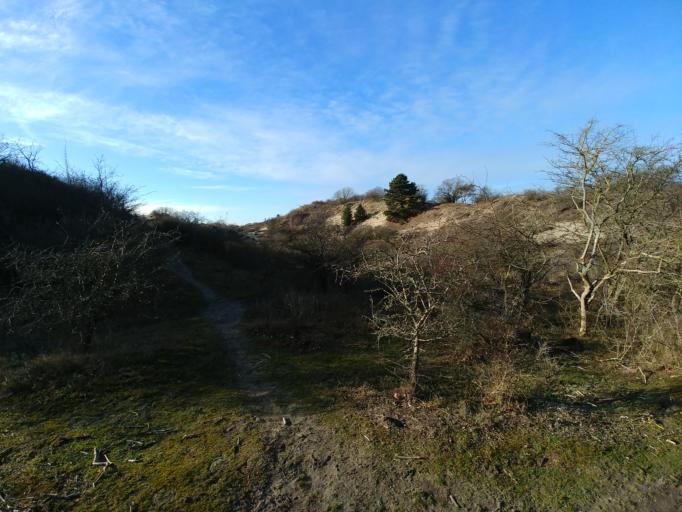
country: NL
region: South Holland
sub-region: Gemeente Den Haag
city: Scheveningen
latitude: 52.1291
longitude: 4.3265
